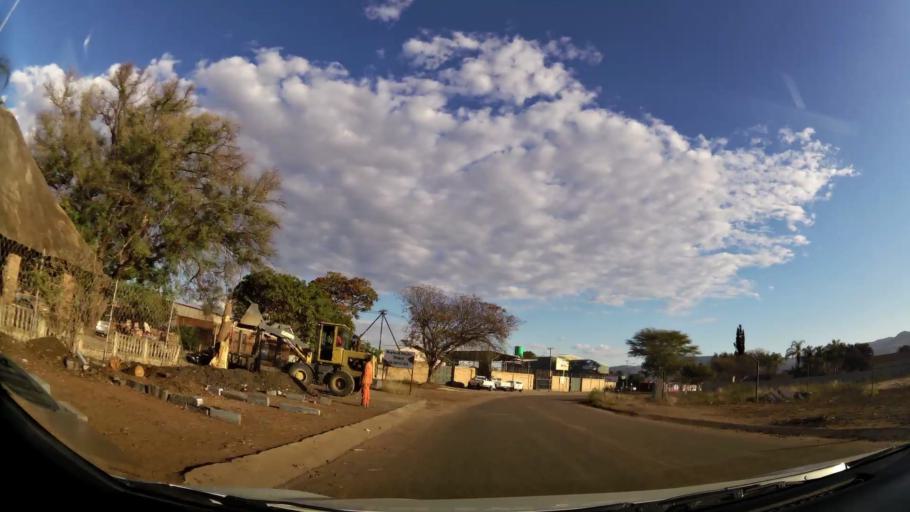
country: ZA
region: Limpopo
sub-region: Waterberg District Municipality
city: Mokopane
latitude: -24.1717
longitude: 29.0023
